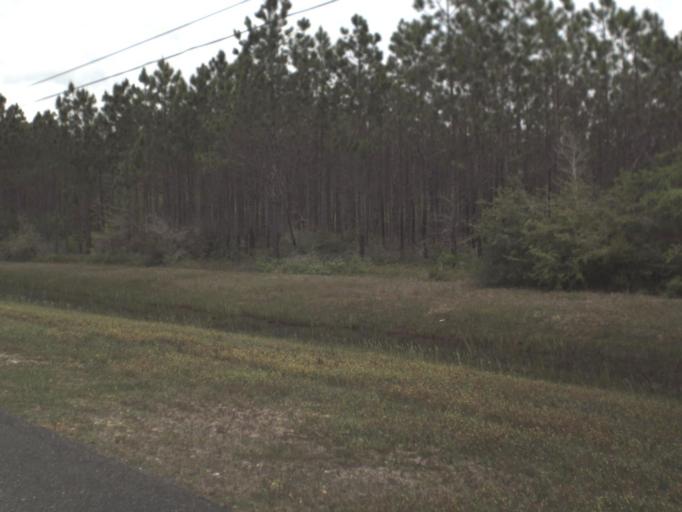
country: US
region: Florida
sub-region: Santa Rosa County
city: Bagdad
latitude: 30.5197
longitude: -87.0873
